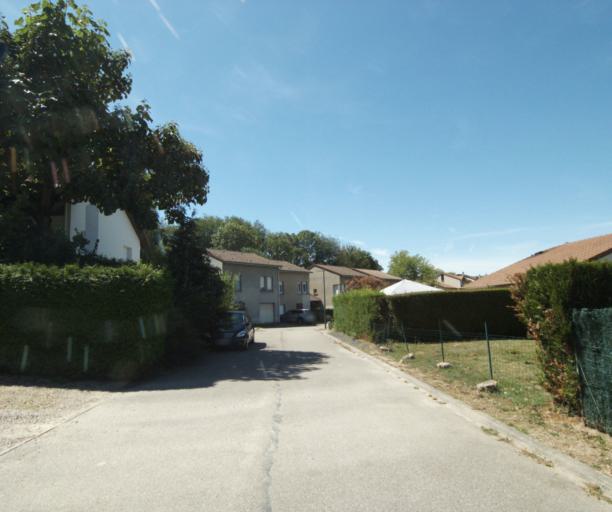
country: FR
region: Lorraine
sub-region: Departement des Vosges
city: Epinal
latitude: 48.1894
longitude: 6.4556
